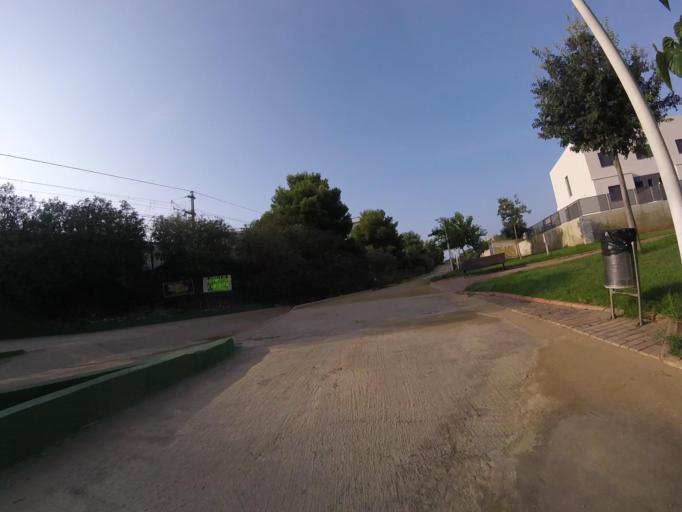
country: ES
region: Valencia
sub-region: Provincia de Castello
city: Orpesa/Oropesa del Mar
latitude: 40.0877
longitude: 0.1380
